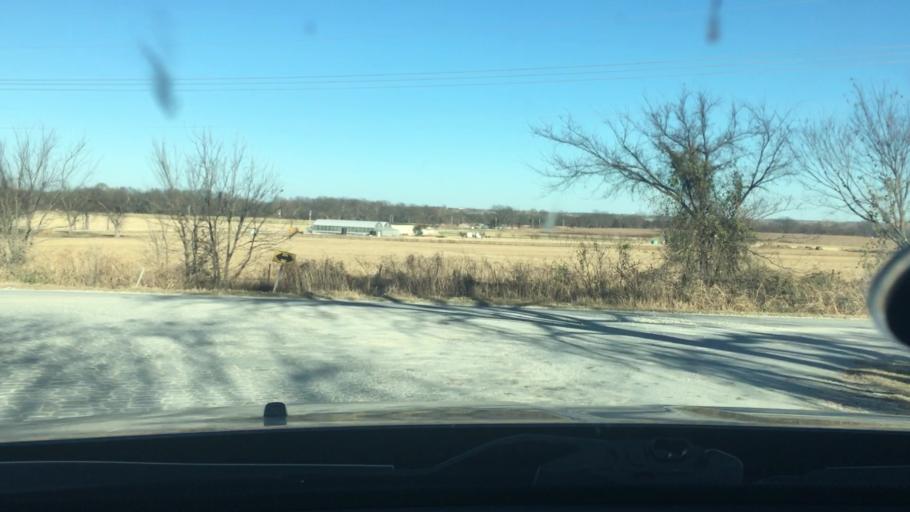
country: US
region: Oklahoma
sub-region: Murray County
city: Davis
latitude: 34.4898
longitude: -97.1577
